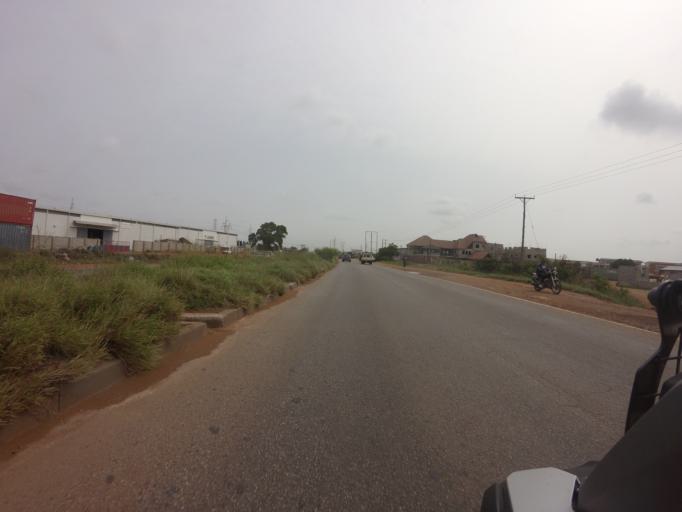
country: GH
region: Greater Accra
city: Tema
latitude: 5.6907
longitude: -0.0071
